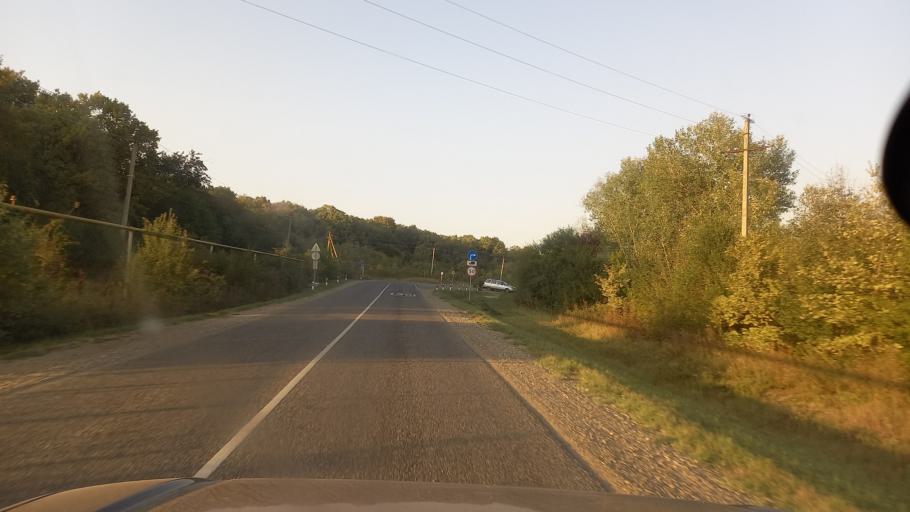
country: RU
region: Krasnodarskiy
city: Smolenskaya
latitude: 44.7605
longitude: 38.7689
